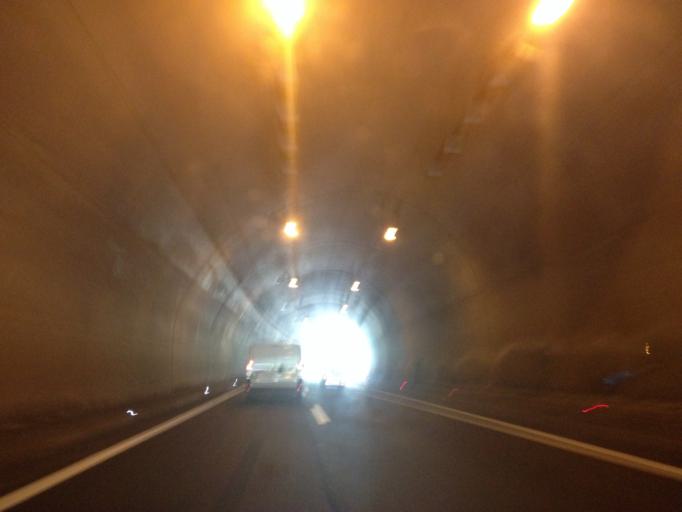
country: AT
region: Lower Austria
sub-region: Politischer Bezirk Neunkirchen
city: Thomasberg
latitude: 47.5707
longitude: 16.1144
